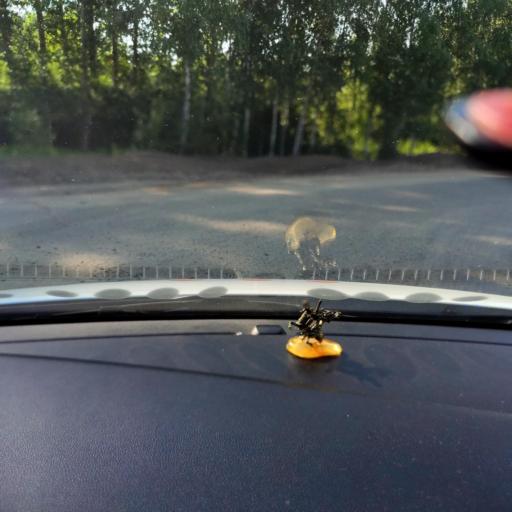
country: RU
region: Tatarstan
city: Stolbishchi
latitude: 55.6990
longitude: 49.2234
